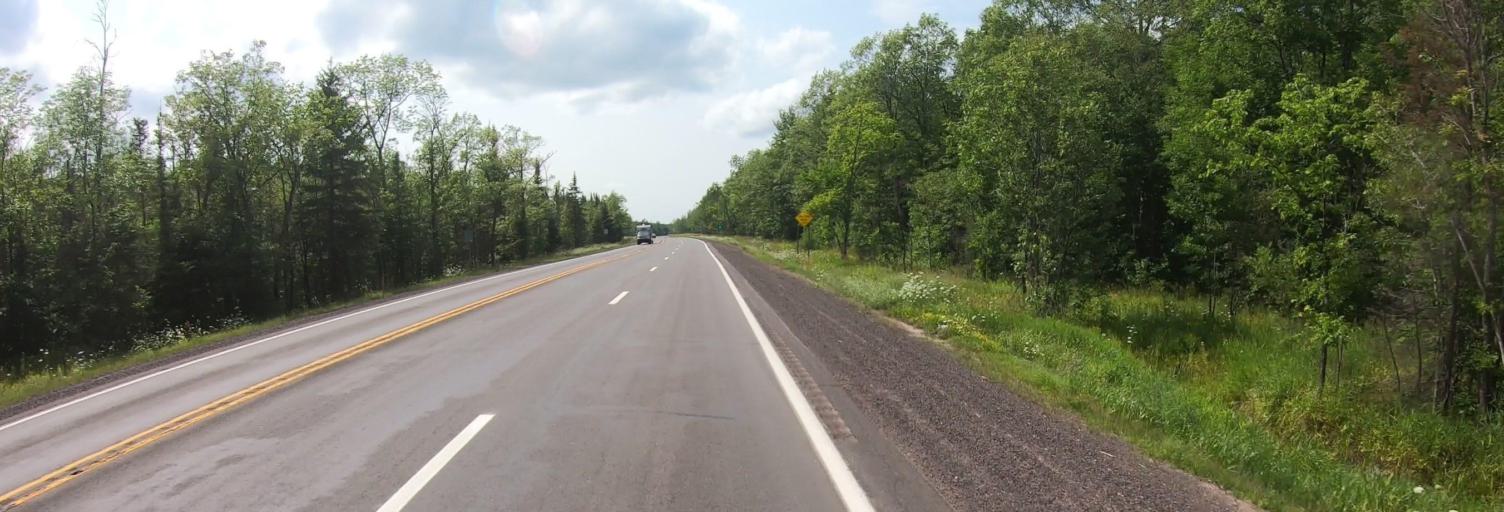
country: US
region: Michigan
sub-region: Ontonagon County
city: Ontonagon
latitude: 46.7792
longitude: -89.0663
